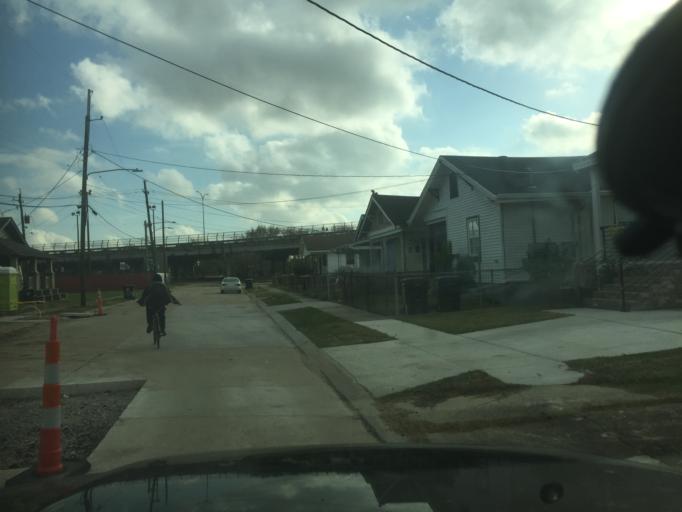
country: US
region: Louisiana
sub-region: Orleans Parish
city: New Orleans
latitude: 29.9935
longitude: -90.0758
